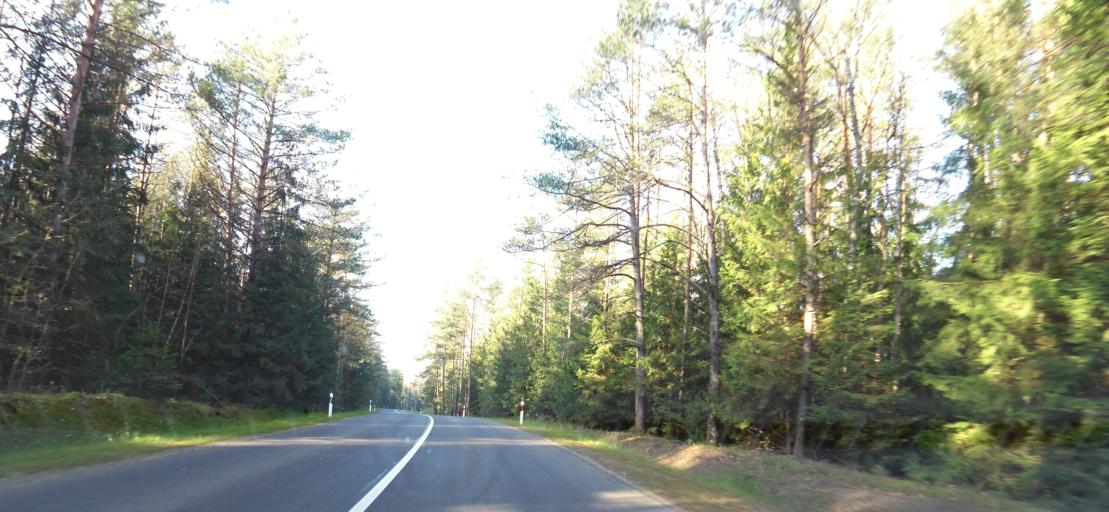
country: LT
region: Vilnius County
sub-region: Trakai
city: Rudiskes
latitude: 54.5100
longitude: 24.8986
